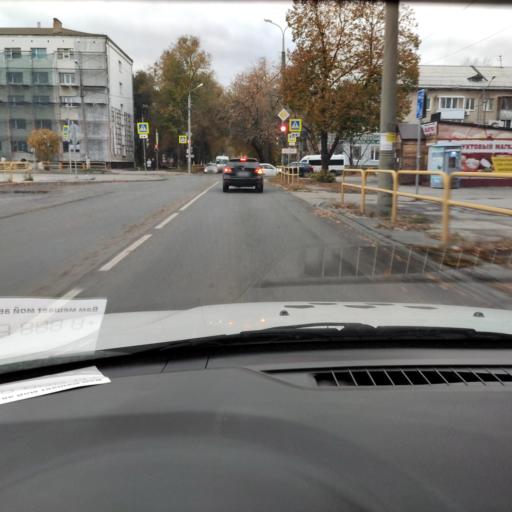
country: RU
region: Samara
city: Tol'yatti
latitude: 53.5043
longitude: 49.4015
